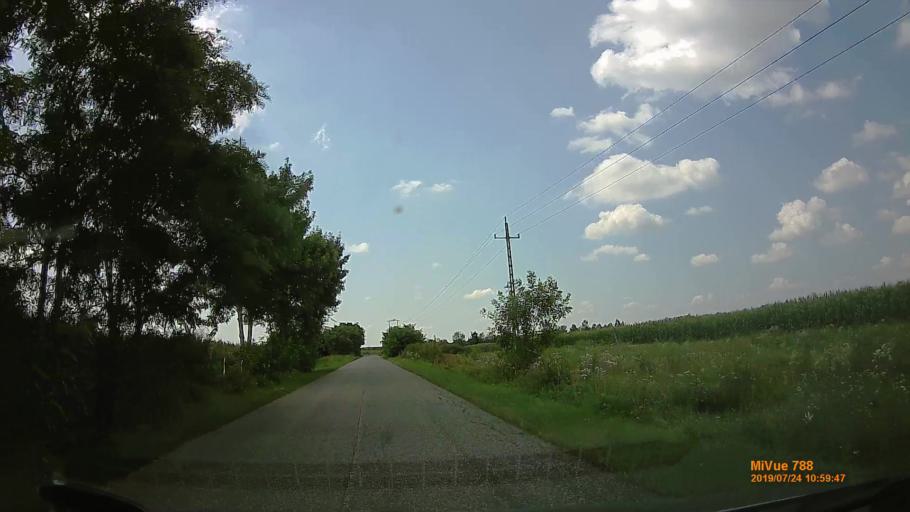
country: HU
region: Szabolcs-Szatmar-Bereg
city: Tarpa
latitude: 48.1622
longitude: 22.5160
